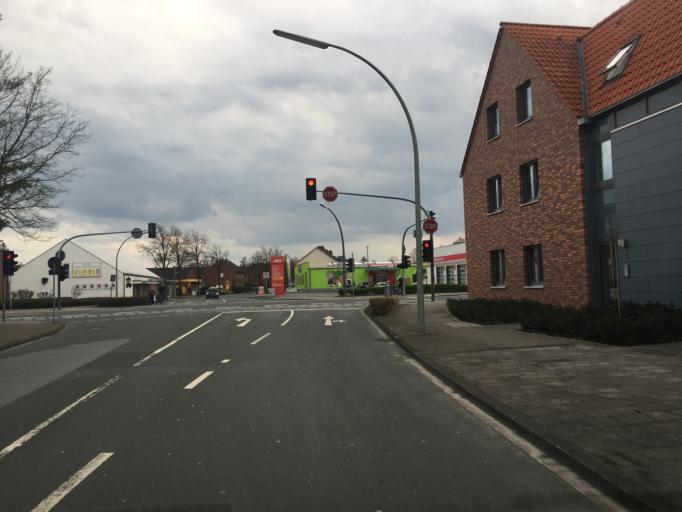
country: DE
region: North Rhine-Westphalia
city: Ludinghausen
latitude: 51.7678
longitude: 7.4316
